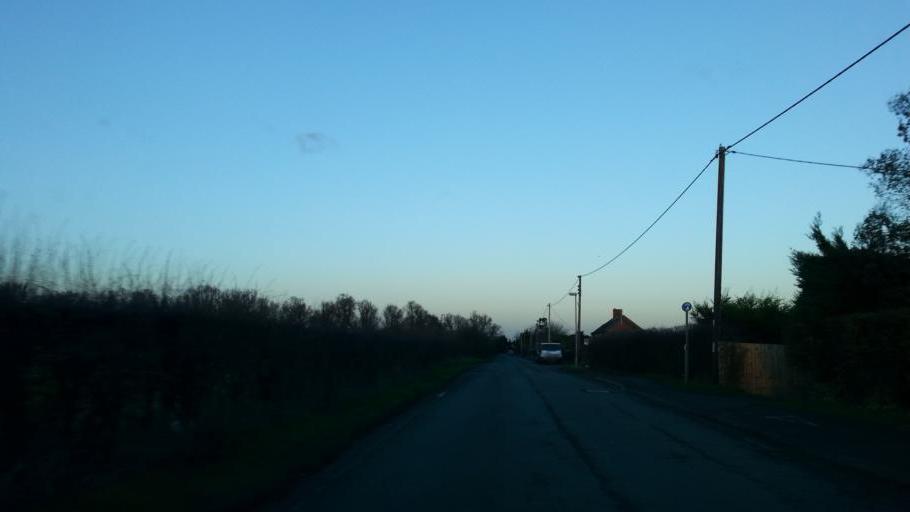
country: GB
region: England
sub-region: Cambridgeshire
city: Needingworth
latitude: 52.2962
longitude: -0.0525
